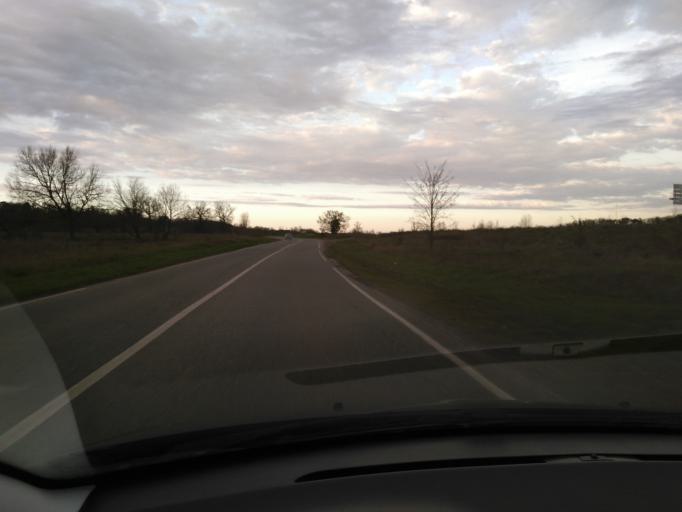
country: FR
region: Midi-Pyrenees
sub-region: Departement de la Haute-Garonne
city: La Salvetat-Saint-Gilles
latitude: 43.5978
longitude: 1.2775
